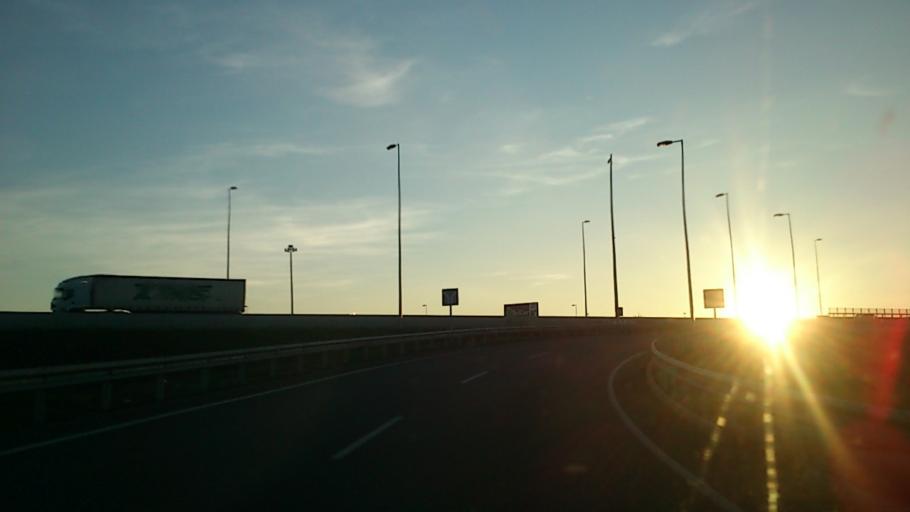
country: ES
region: Madrid
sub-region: Provincia de Madrid
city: Alcala de Henares
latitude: 40.5021
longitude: -3.3385
